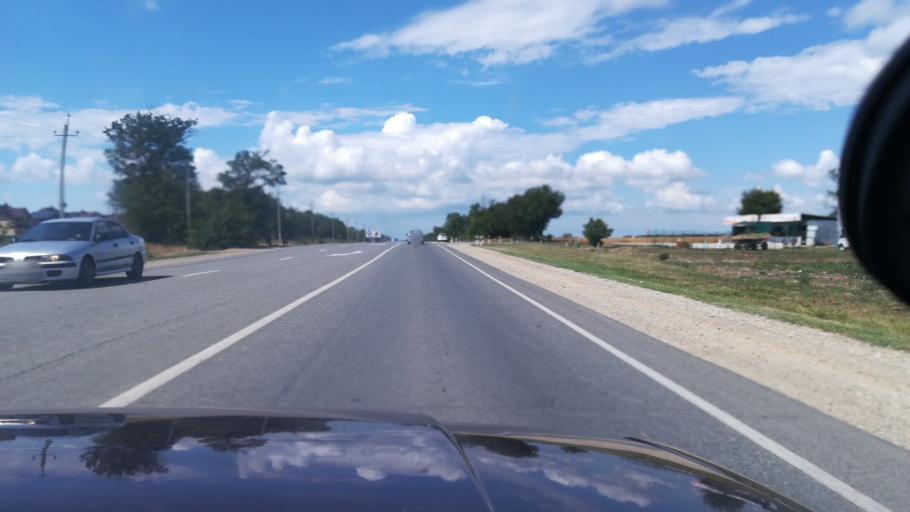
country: RU
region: Krasnodarskiy
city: Tsibanobalka
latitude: 44.9838
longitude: 37.3220
